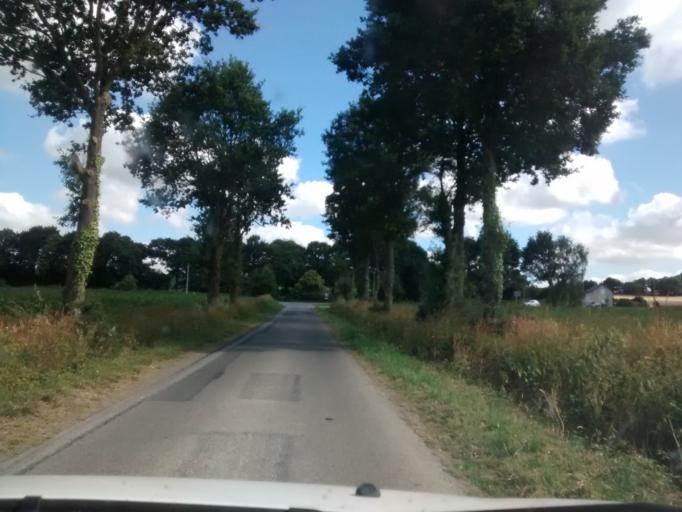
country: FR
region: Brittany
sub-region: Departement d'Ille-et-Vilaine
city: Bain-de-Bretagne
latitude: 47.8416
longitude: -1.7115
